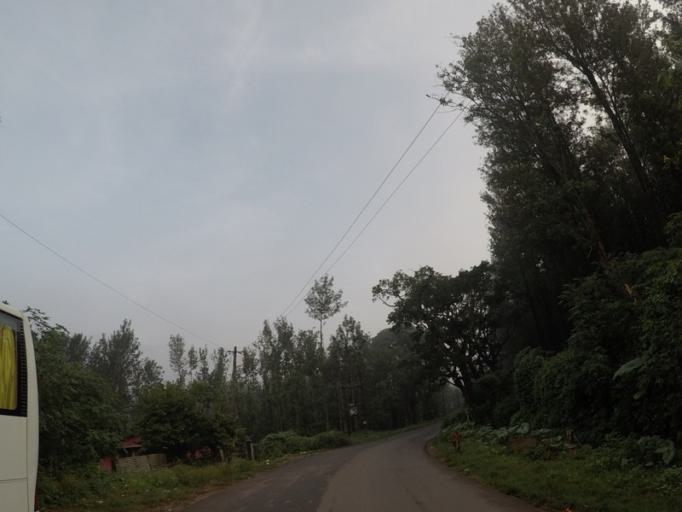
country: IN
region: Karnataka
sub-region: Chikmagalur
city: Chikmagalur
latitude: 13.3729
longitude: 75.7443
